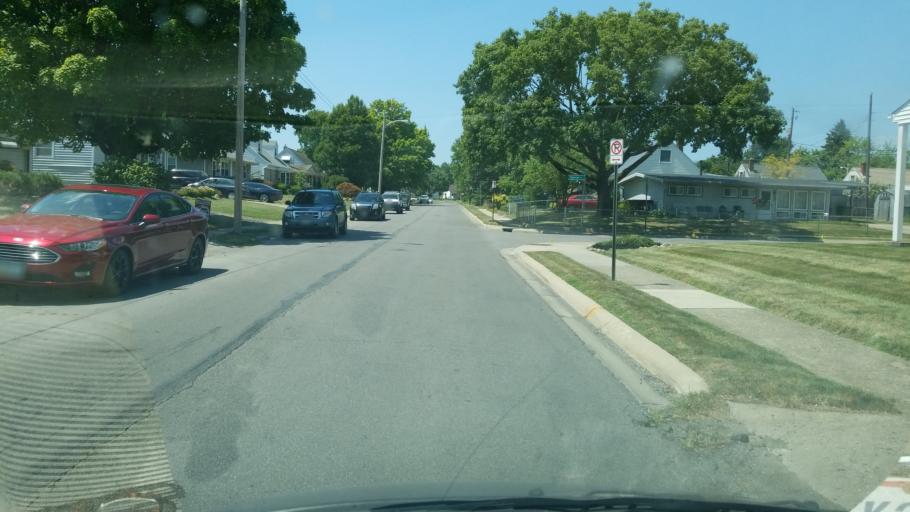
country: US
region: Ohio
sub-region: Franklin County
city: Lincoln Village
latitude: 39.9381
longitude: -83.1080
